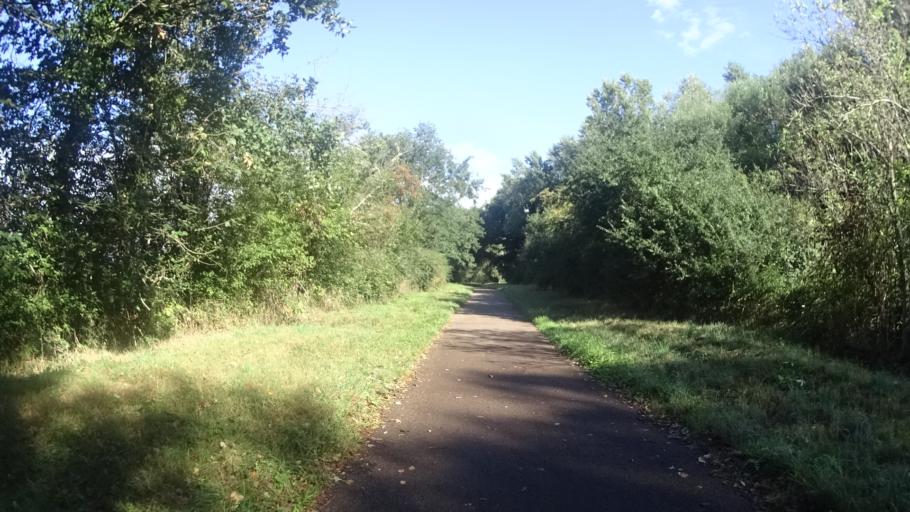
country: FR
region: Bourgogne
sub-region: Departement de la Nievre
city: Pouilly-sur-Loire
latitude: 47.2985
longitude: 2.9202
